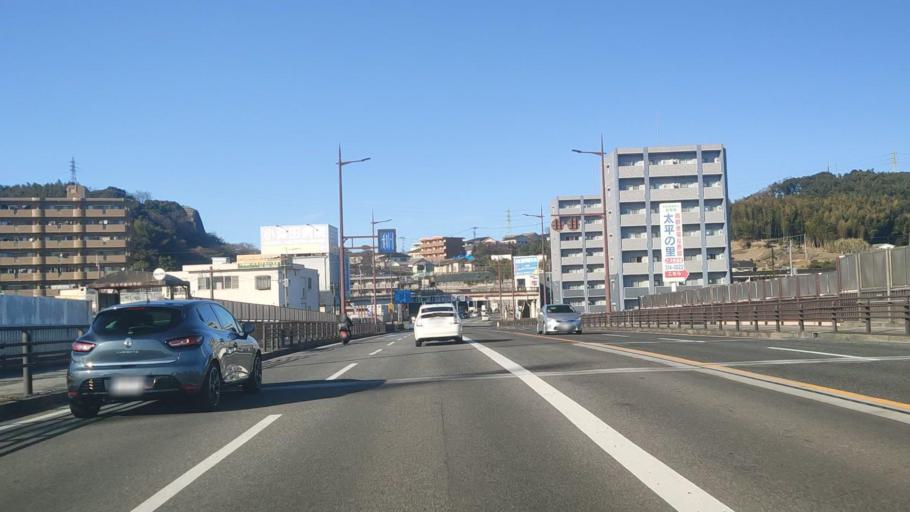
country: JP
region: Oita
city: Oita
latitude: 33.2170
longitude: 131.5953
